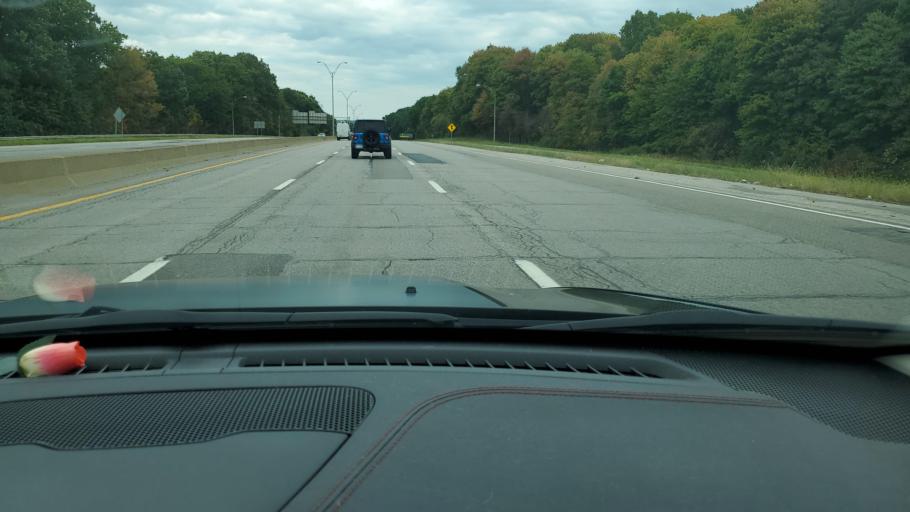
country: US
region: Ohio
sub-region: Mahoning County
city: Struthers
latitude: 41.0616
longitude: -80.6277
